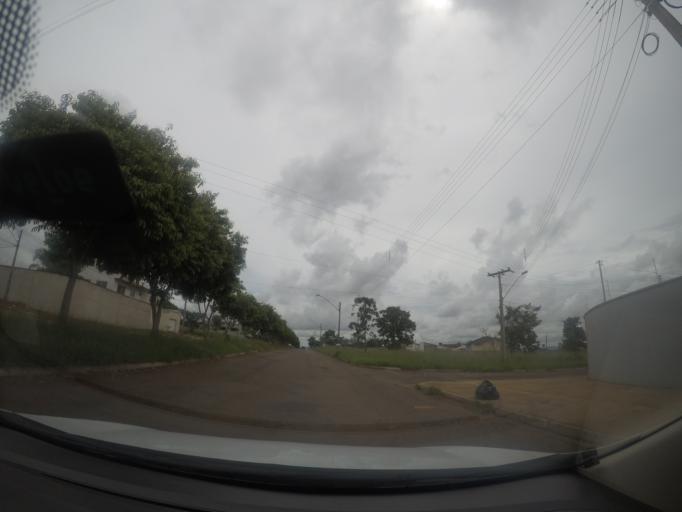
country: BR
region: Goias
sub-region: Trindade
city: Trindade
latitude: -16.6904
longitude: -49.3881
